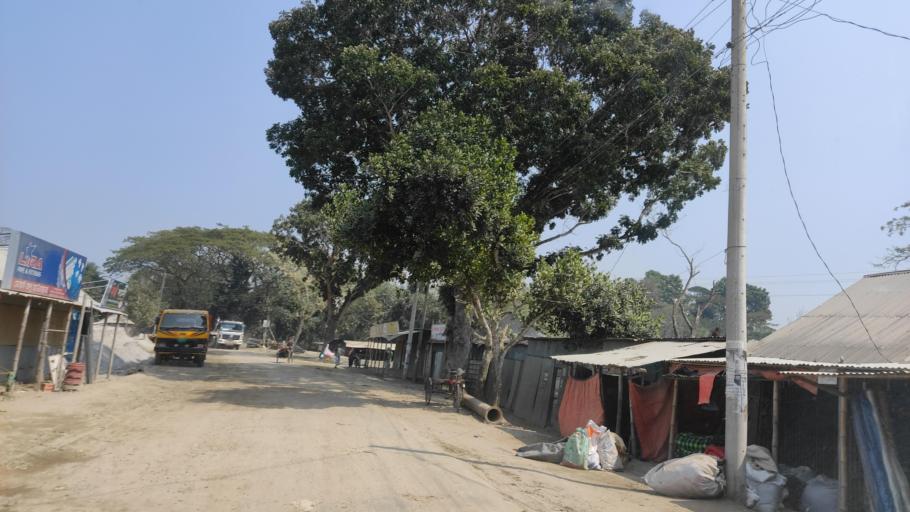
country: BD
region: Khulna
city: Kalia
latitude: 23.1953
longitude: 89.6953
